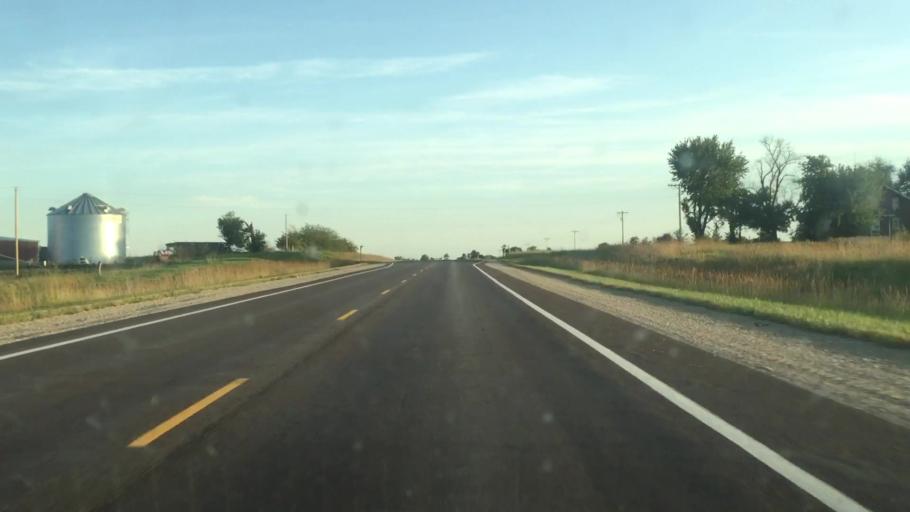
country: US
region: Kansas
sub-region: Atchison County
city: Atchison
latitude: 39.4423
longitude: -95.0932
